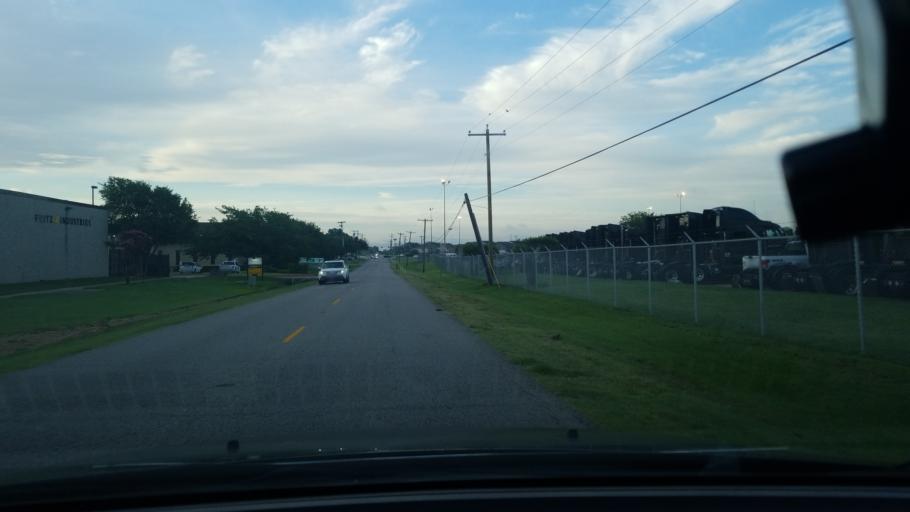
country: US
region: Texas
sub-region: Dallas County
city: Balch Springs
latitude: 32.7708
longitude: -96.6530
